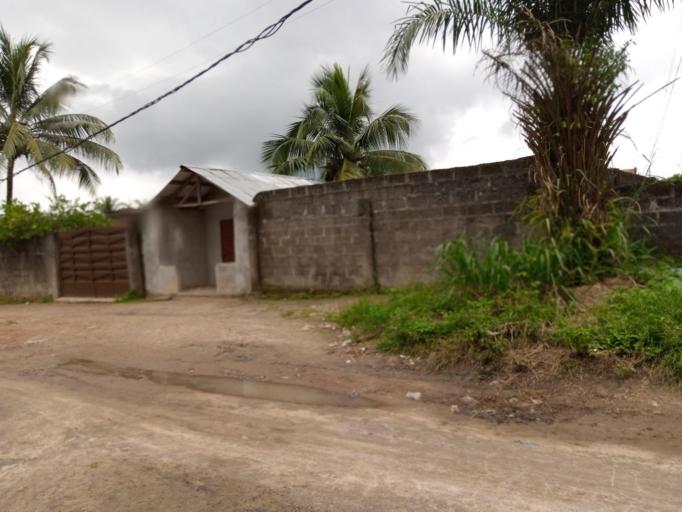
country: SL
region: Eastern Province
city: Kenema
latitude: 7.8565
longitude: -11.1990
